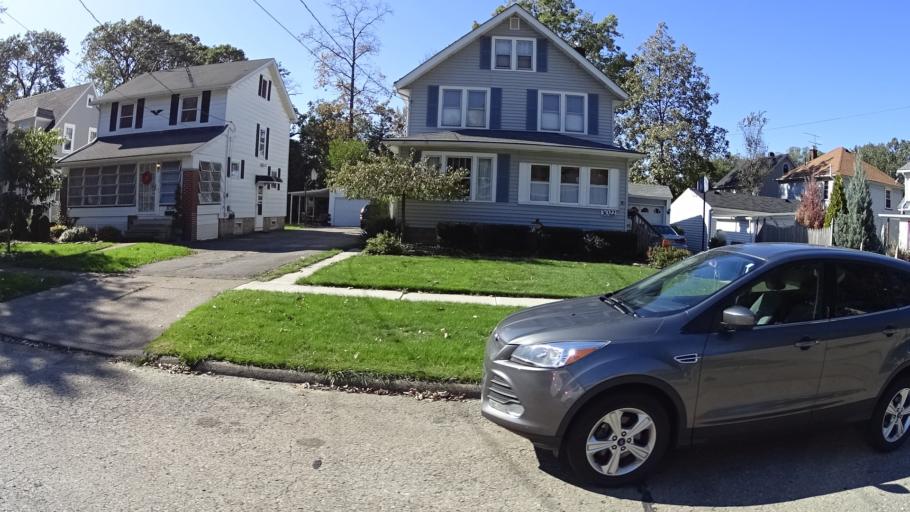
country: US
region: Ohio
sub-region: Lorain County
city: Lorain
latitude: 41.4421
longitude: -82.1730
